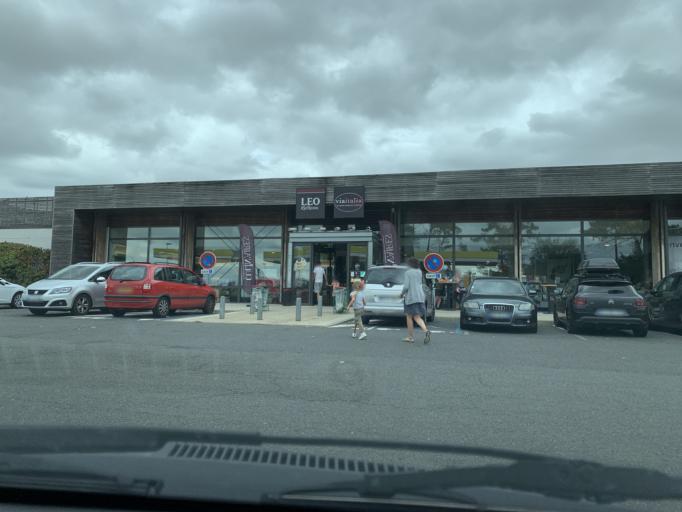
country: FR
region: Centre
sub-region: Departement d'Indre-et-Loire
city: Athee-sur-Cher
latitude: 47.3023
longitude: 0.8893
